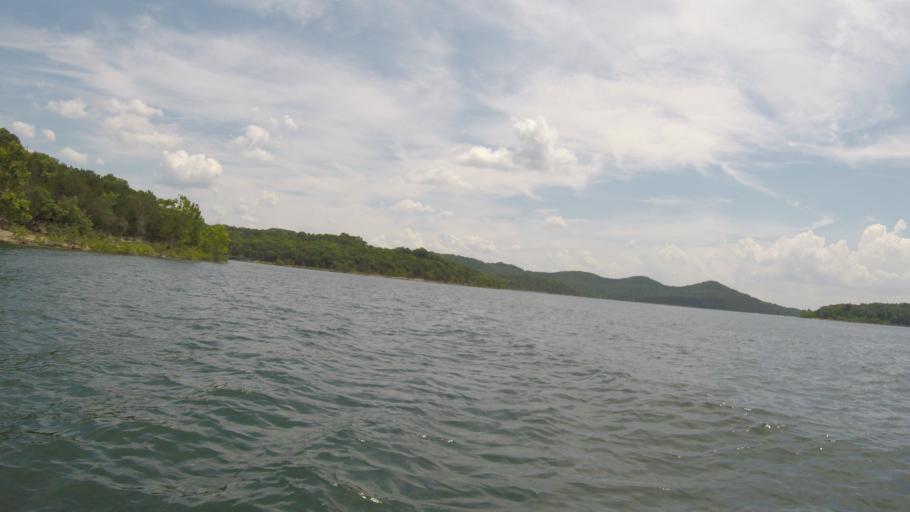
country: US
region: Missouri
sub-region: Barry County
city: Shell Knob
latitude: 36.6180
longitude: -93.5488
